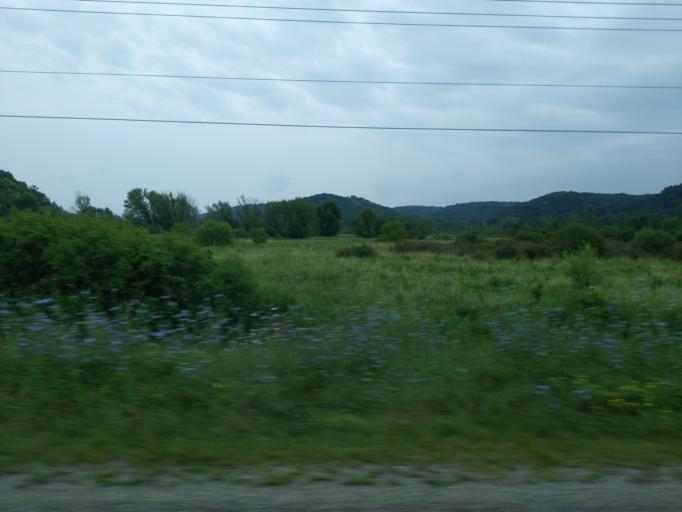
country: US
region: Wisconsin
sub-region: Dane County
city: Mazomanie
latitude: 43.2022
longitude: -89.7516
